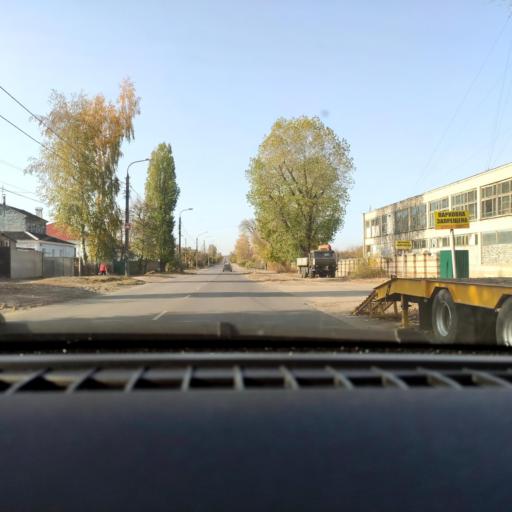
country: RU
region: Voronezj
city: Maslovka
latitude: 51.6103
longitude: 39.2305
